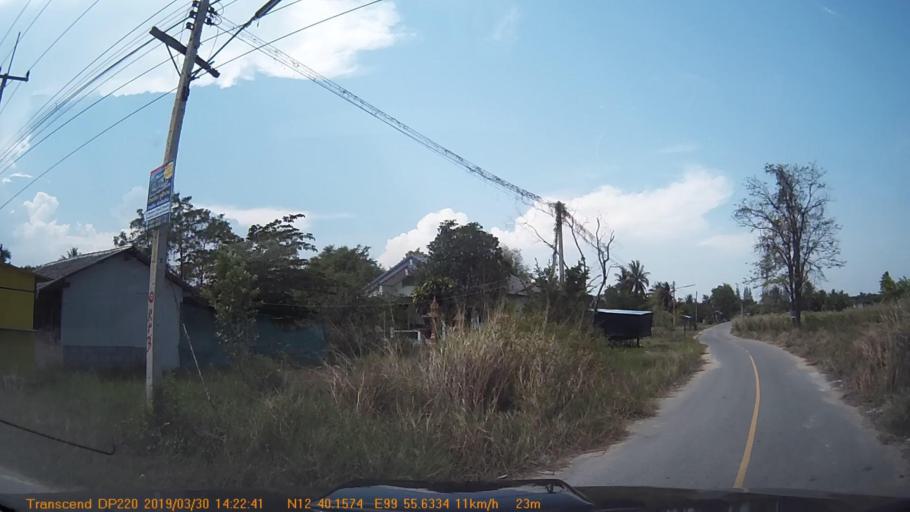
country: TH
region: Prachuap Khiri Khan
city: Hua Hin
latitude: 12.6695
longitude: 99.9272
